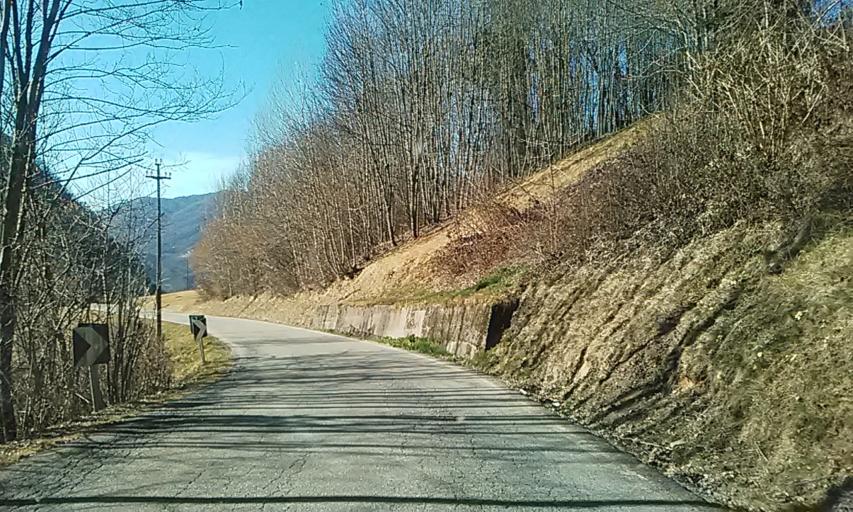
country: IT
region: Piedmont
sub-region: Provincia di Vercelli
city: Breia
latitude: 45.7799
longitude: 8.2892
